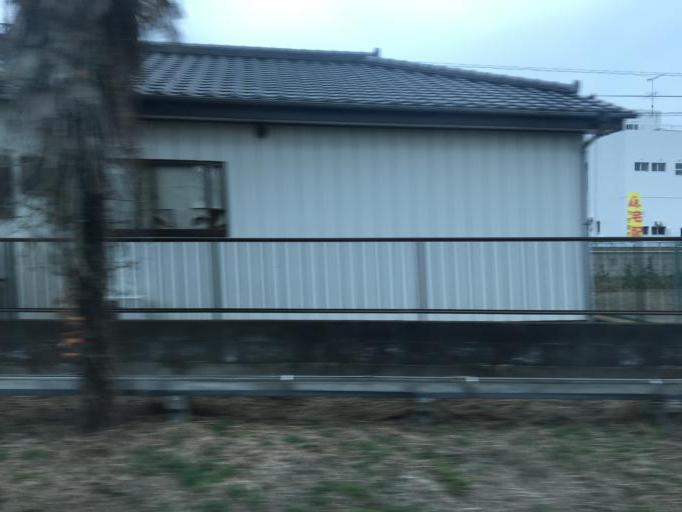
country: JP
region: Ibaraki
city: Yuki
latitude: 36.2973
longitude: 139.8788
